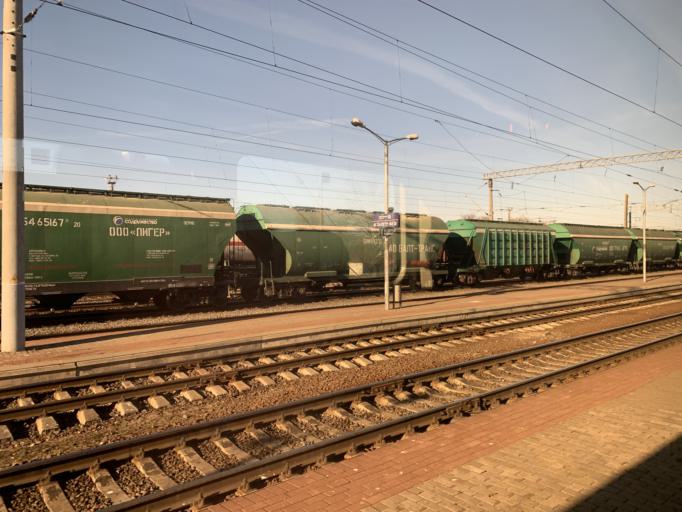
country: BY
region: Minsk
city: Maladzyechna
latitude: 54.3163
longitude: 26.8341
